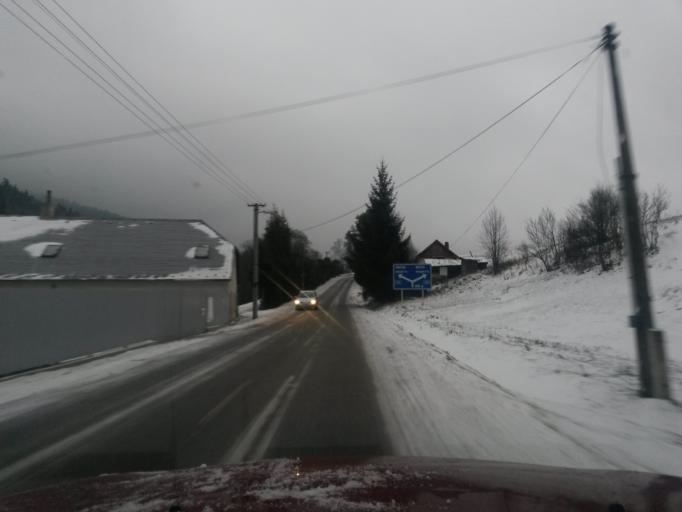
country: SK
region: Kosicky
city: Medzev
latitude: 48.7275
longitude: 20.7221
